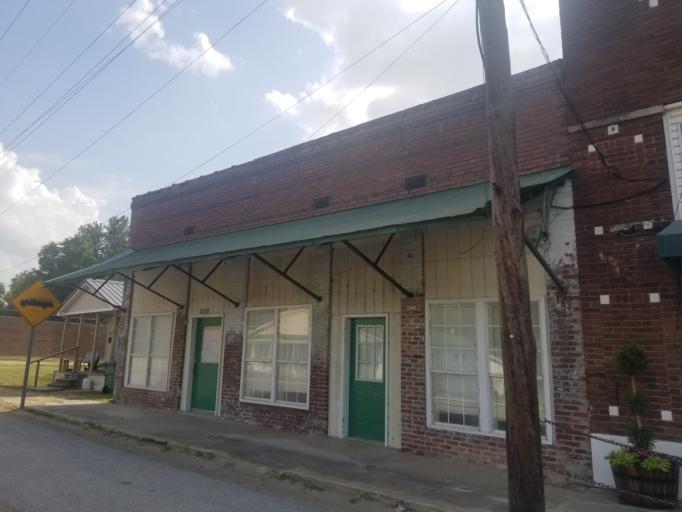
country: US
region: Arkansas
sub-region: Crittenden County
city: Marion
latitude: 35.2275
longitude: -90.3264
